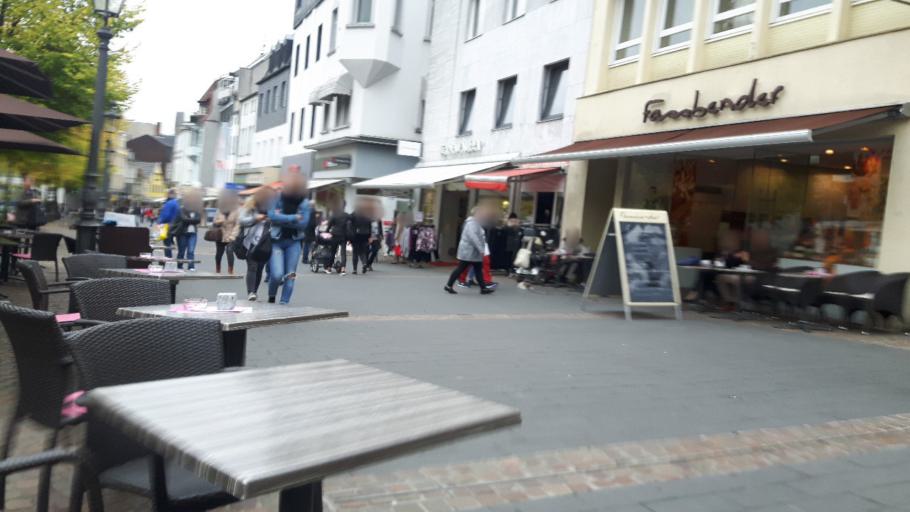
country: DE
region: North Rhine-Westphalia
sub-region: Regierungsbezirk Koln
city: Siegburg
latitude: 50.7971
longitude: 7.2073
